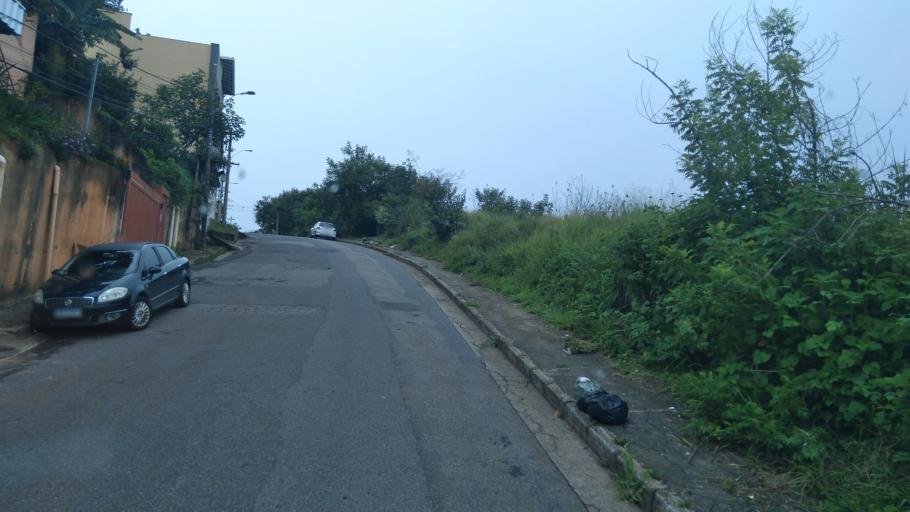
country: BR
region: Minas Gerais
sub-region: Belo Horizonte
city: Belo Horizonte
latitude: -19.9136
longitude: -43.8850
